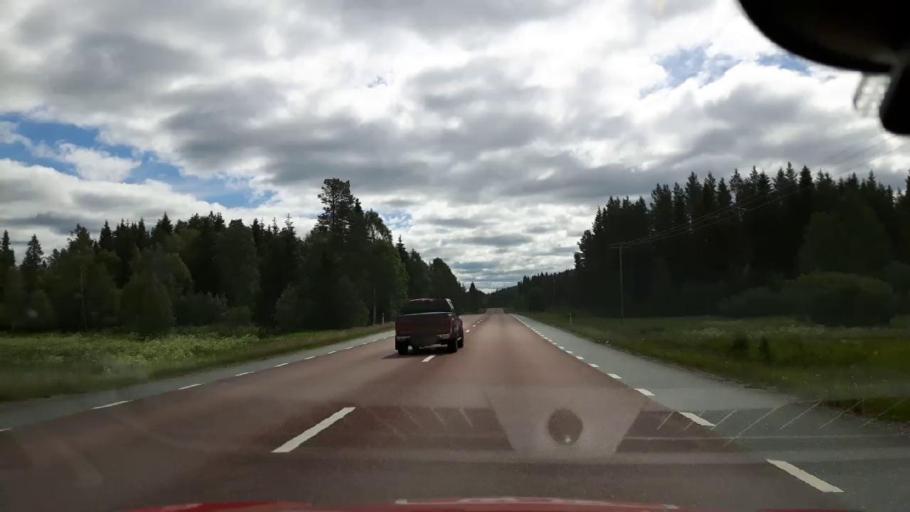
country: SE
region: Jaemtland
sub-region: Braecke Kommun
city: Braecke
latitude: 62.9431
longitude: 15.1793
